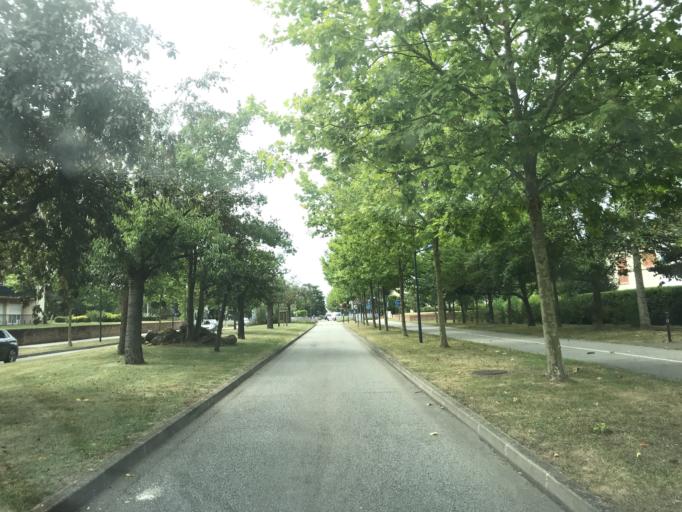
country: FR
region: Ile-de-France
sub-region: Departement des Yvelines
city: Maurepas
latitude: 48.7647
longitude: 1.9391
